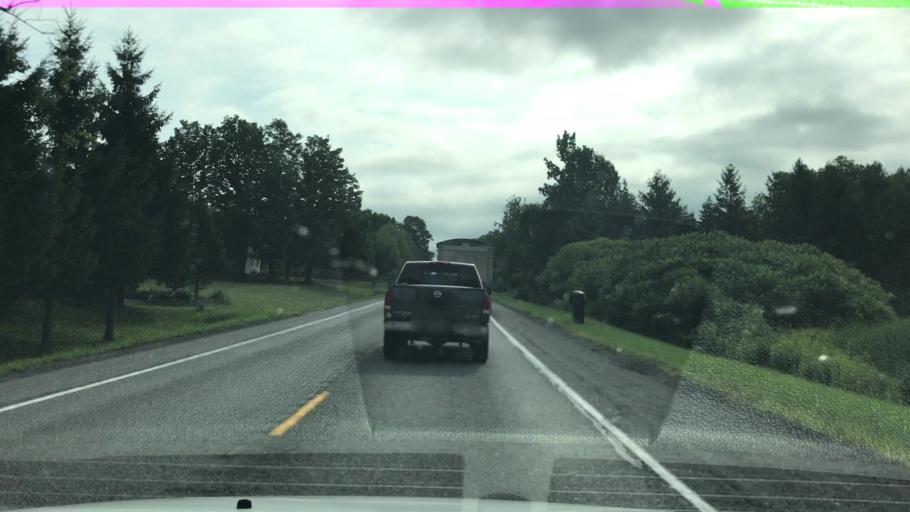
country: US
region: New York
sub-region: Erie County
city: Alden
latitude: 42.8353
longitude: -78.4207
